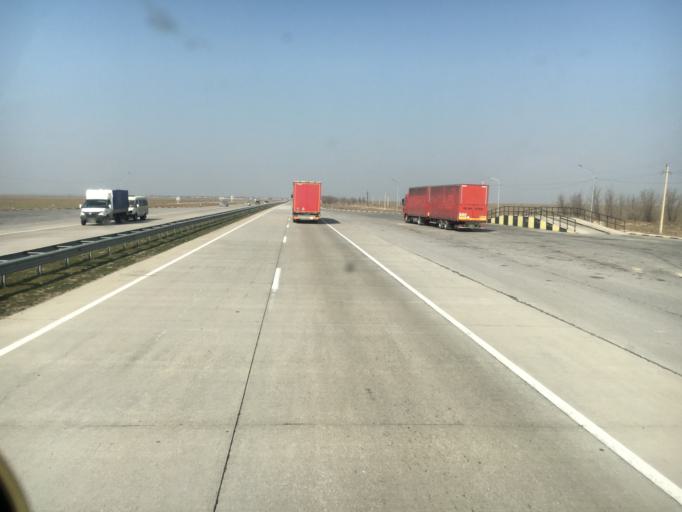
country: KZ
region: Ongtustik Qazaqstan
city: Temirlanovka
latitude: 42.8453
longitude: 69.0958
